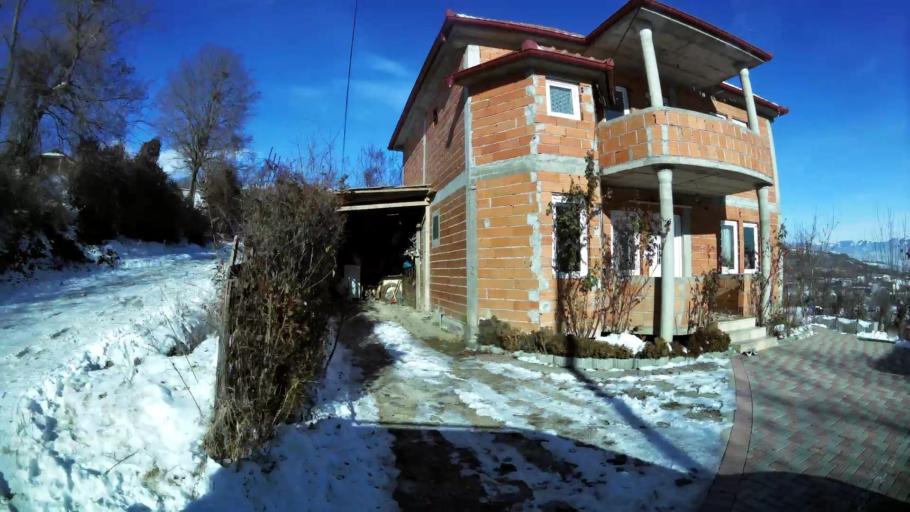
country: MK
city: Ljubin
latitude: 41.9796
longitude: 21.3014
